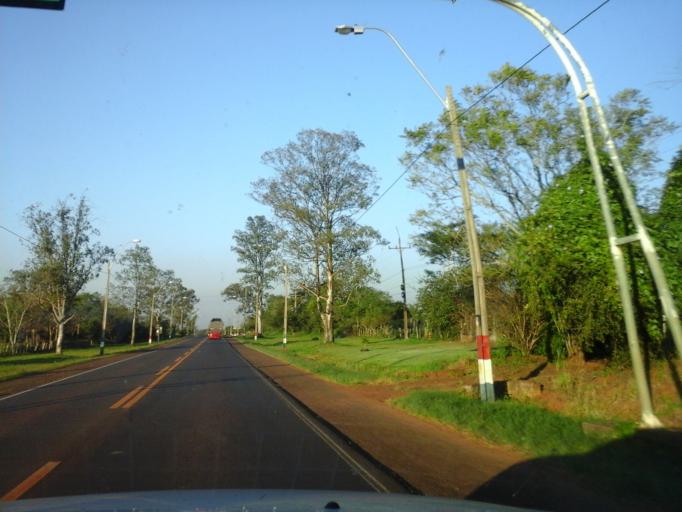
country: PY
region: Itapua
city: General Delgado
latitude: -27.0900
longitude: -56.5150
